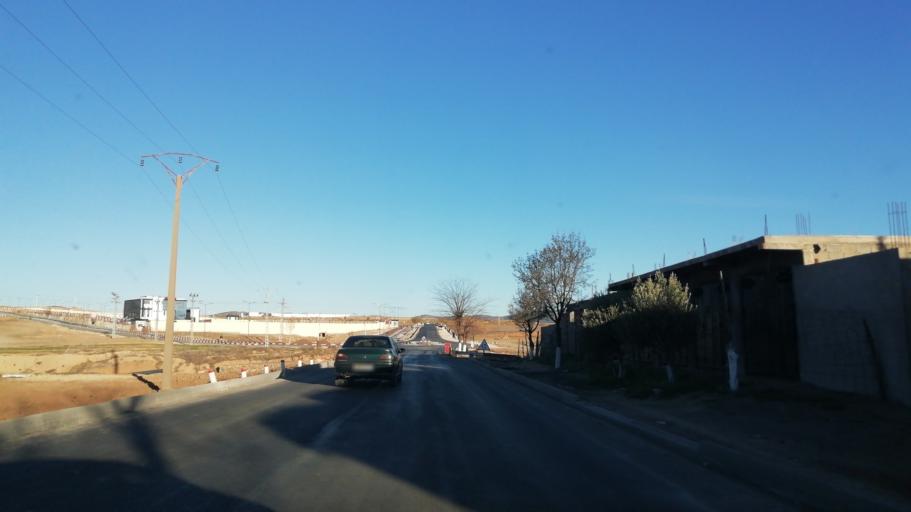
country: DZ
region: Tlemcen
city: Sebdou
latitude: 34.6553
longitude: -1.3114
